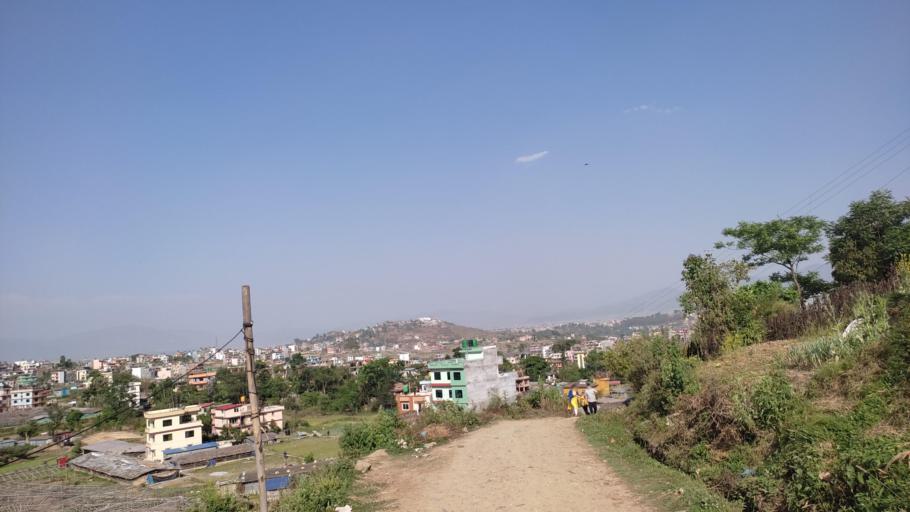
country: NP
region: Central Region
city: Kirtipur
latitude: 27.6603
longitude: 85.2608
